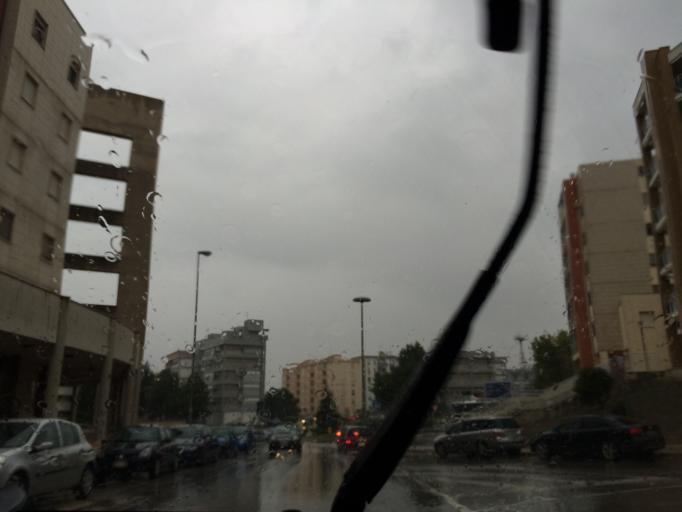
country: IT
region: Basilicate
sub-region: Provincia di Matera
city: Matera
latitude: 40.6728
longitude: 16.5870
